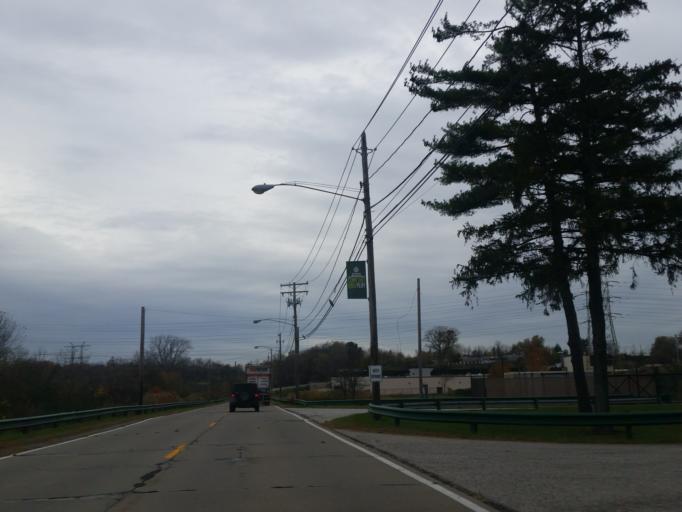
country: US
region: Ohio
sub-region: Cuyahoga County
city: Newburgh Heights
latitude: 41.4225
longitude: -81.6497
